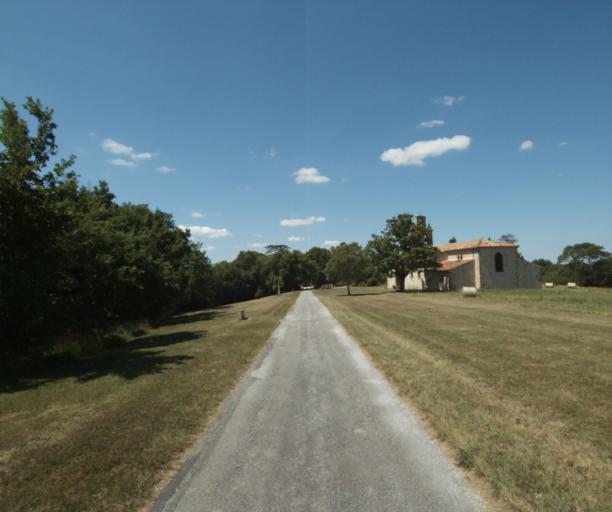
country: FR
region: Midi-Pyrenees
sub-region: Departement de la Haute-Garonne
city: Saint-Felix-Lauragais
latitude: 43.4774
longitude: 1.8612
